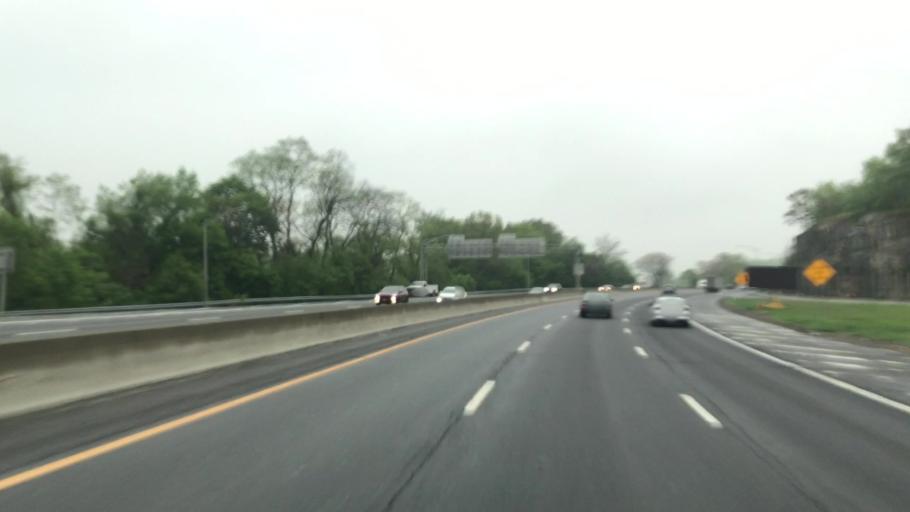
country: US
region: New York
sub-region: Westchester County
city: Bronxville
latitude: 40.9559
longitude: -73.8611
